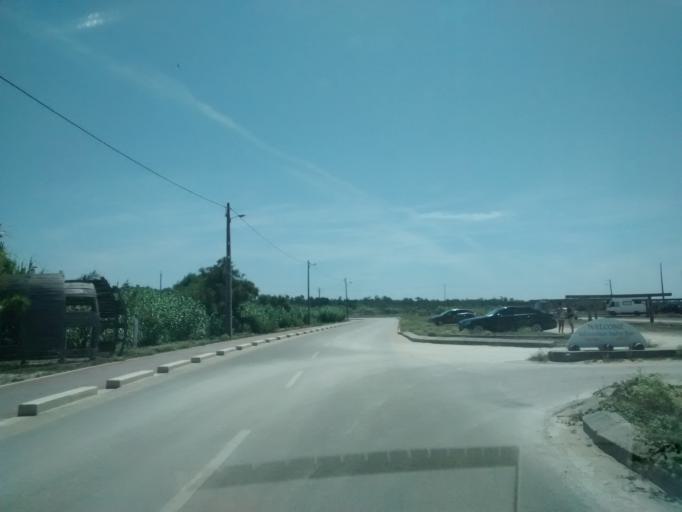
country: PT
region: Coimbra
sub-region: Mira
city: Mira
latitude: 40.4466
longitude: -8.8042
